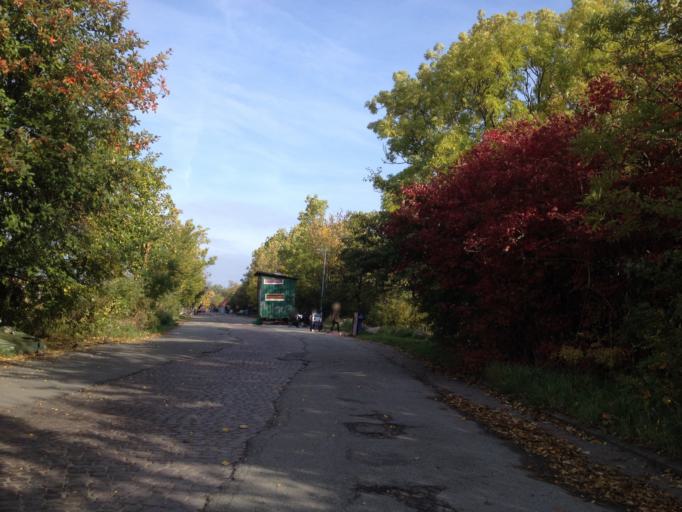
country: DK
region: Capital Region
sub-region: Kobenhavn
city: Christianshavn
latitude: 55.6812
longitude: 12.6101
